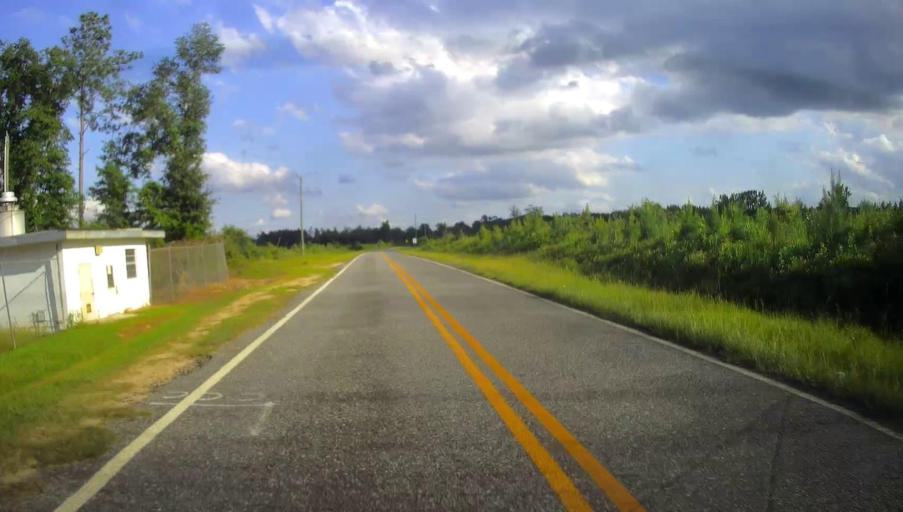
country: US
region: Georgia
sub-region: Crawford County
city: Roberta
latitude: 32.7093
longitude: -84.0174
